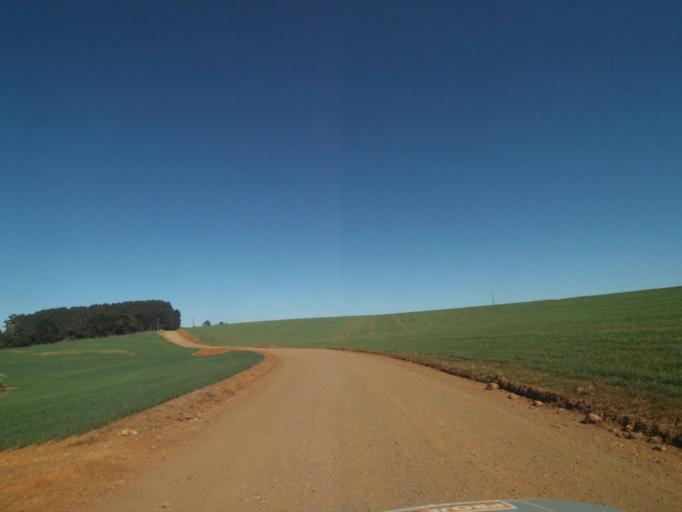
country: BR
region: Parana
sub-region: Tibagi
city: Tibagi
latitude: -24.6087
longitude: -50.6059
